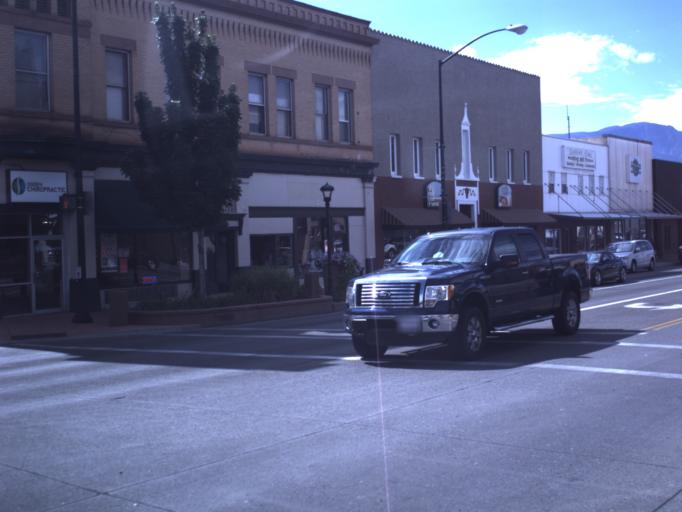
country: US
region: Utah
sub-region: Sevier County
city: Richfield
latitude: 38.7681
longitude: -112.0849
